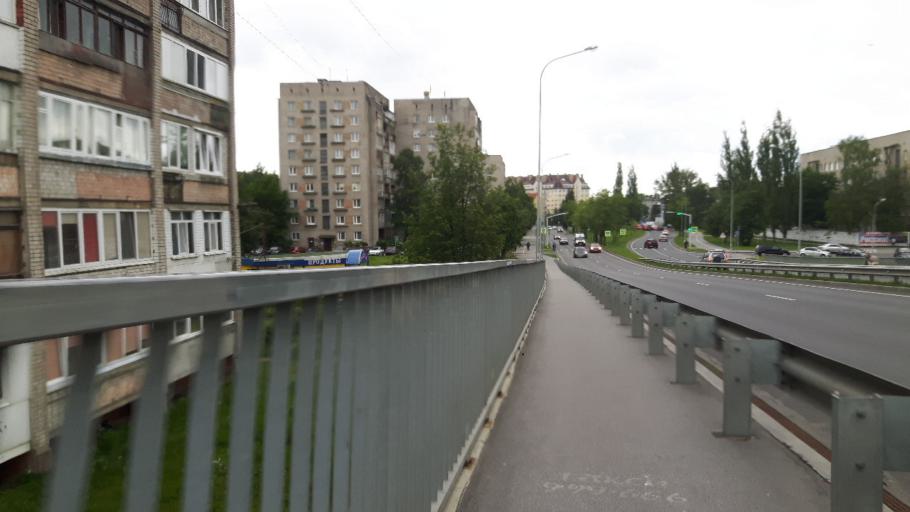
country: RU
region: Kaliningrad
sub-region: Gorod Kaliningrad
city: Kaliningrad
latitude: 54.7339
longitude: 20.4921
